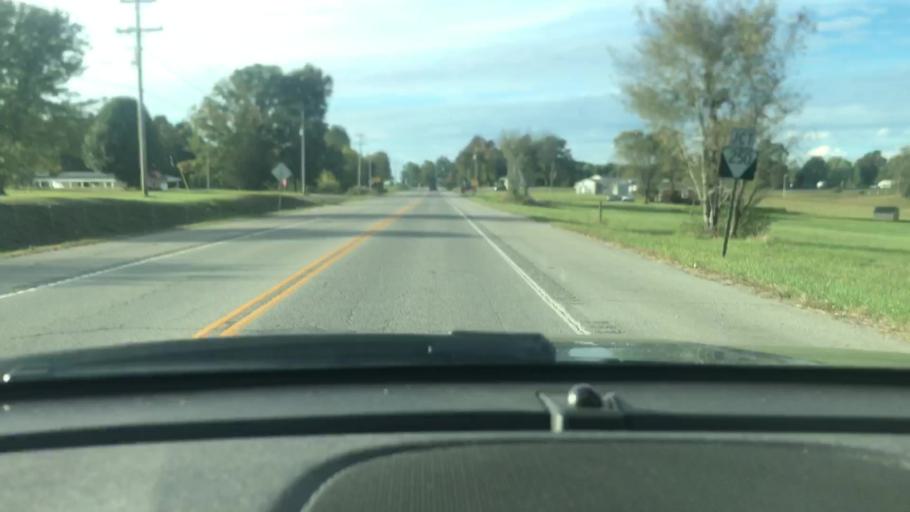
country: US
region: Tennessee
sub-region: Dickson County
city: White Bluff
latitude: 36.1358
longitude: -87.2377
